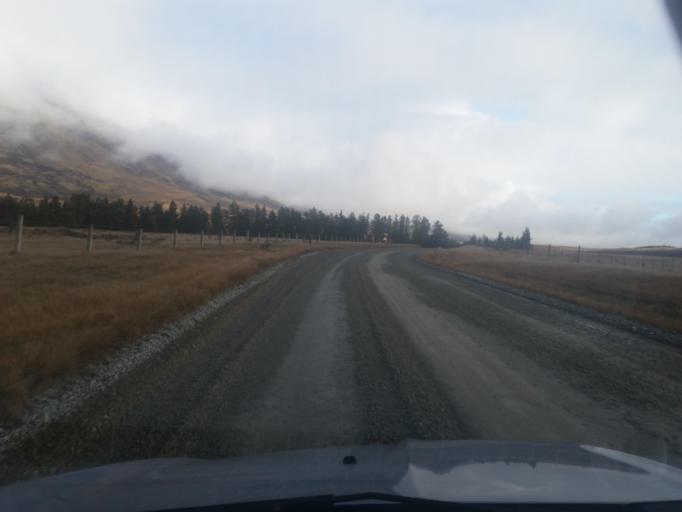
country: NZ
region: Canterbury
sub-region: Ashburton District
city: Methven
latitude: -43.6144
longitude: 171.0681
